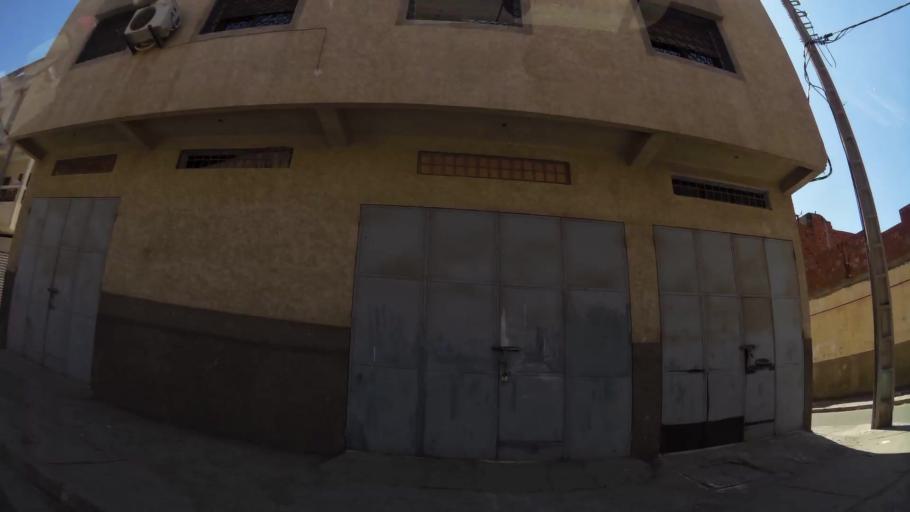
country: MA
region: Gharb-Chrarda-Beni Hssen
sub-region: Kenitra Province
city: Kenitra
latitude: 34.2398
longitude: -6.5519
